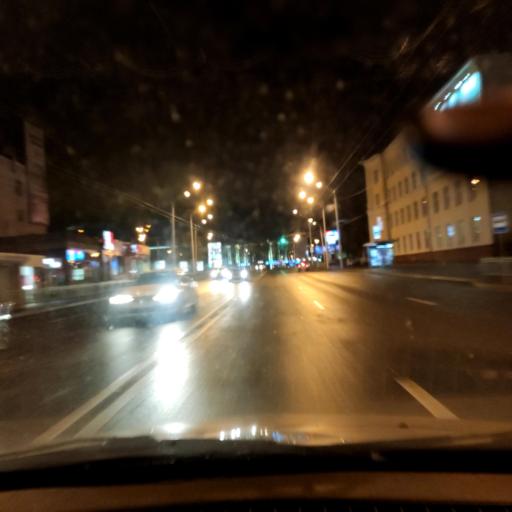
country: RU
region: Bashkortostan
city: Ufa
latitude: 54.7374
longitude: 55.9815
